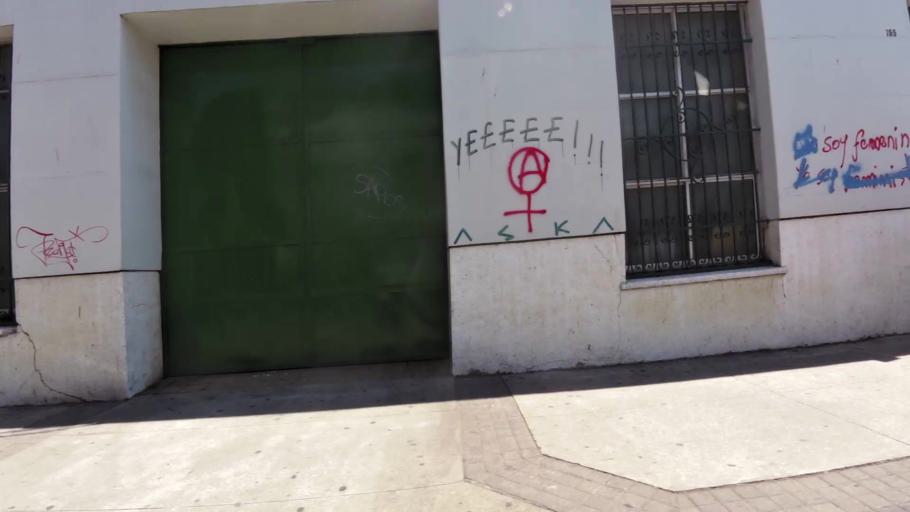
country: CL
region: Biobio
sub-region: Provincia de Concepcion
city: Concepcion
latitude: -36.8232
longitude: -73.0504
